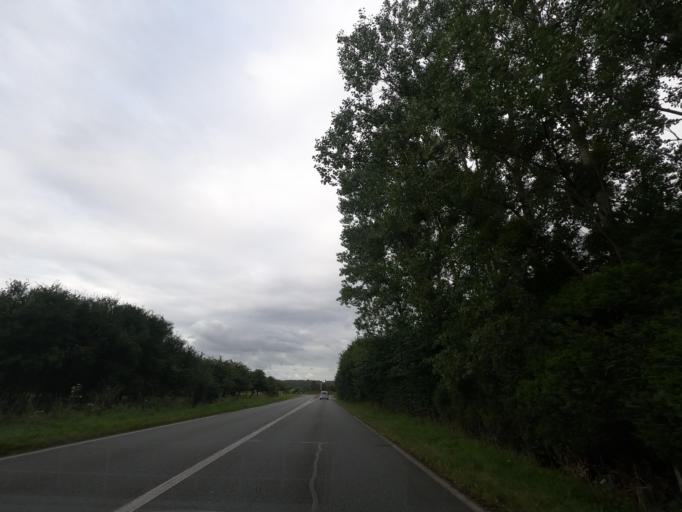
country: FR
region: Haute-Normandie
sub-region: Departement de l'Eure
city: Bourgtheroulde-Infreville
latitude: 49.2702
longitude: 0.8161
